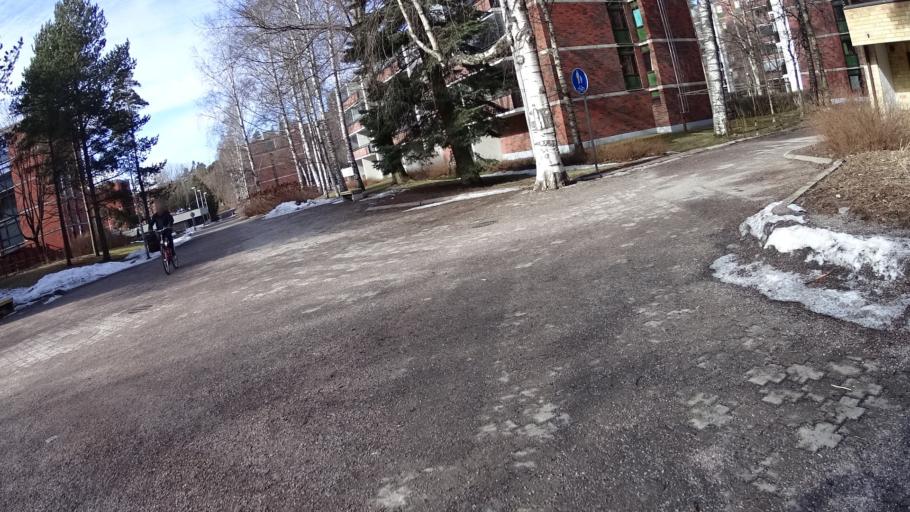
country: FI
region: Uusimaa
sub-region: Helsinki
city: Kilo
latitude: 60.2277
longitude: 24.8170
